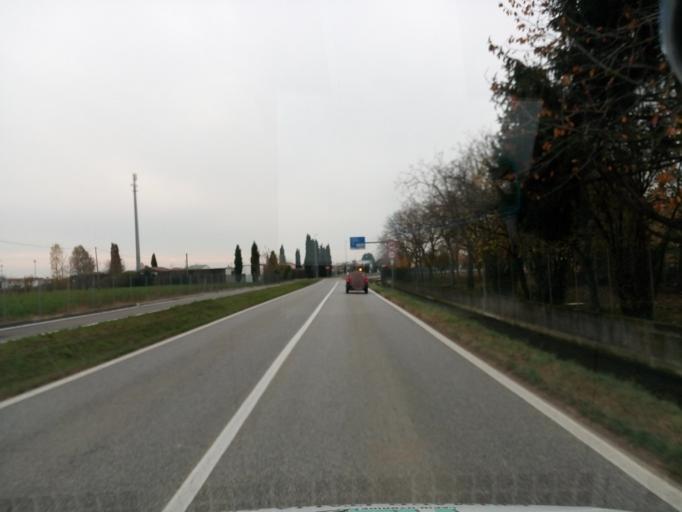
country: IT
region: Veneto
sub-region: Provincia di Treviso
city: Vedelago
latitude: 45.6944
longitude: 12.0174
